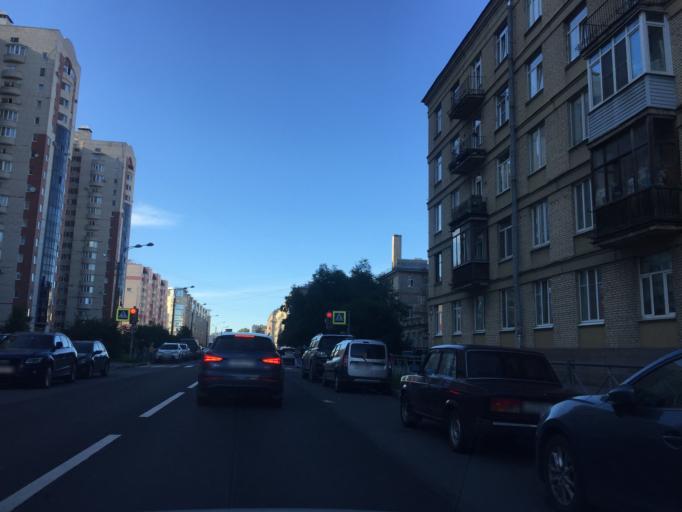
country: RU
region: St.-Petersburg
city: Admiralteisky
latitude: 59.8728
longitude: 30.3137
